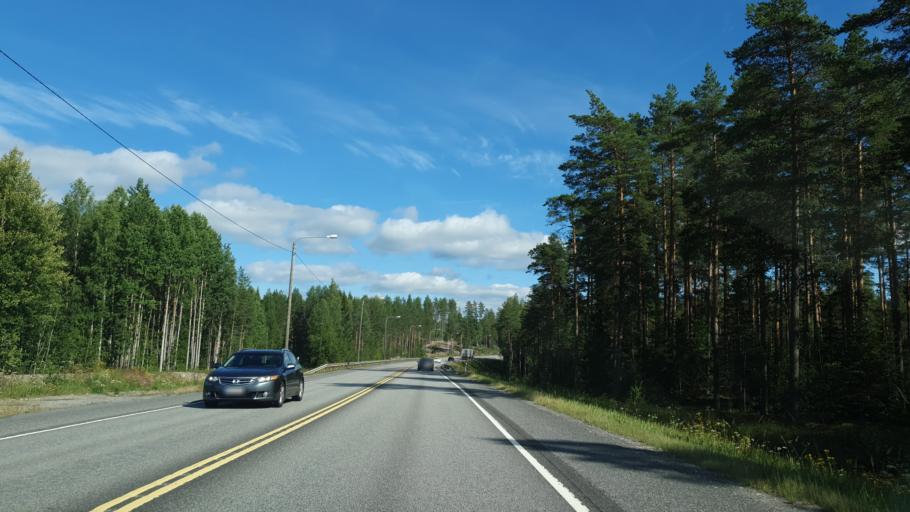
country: FI
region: Central Finland
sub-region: Jyvaeskylae
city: Toivakka
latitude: 62.2512
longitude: 26.1172
